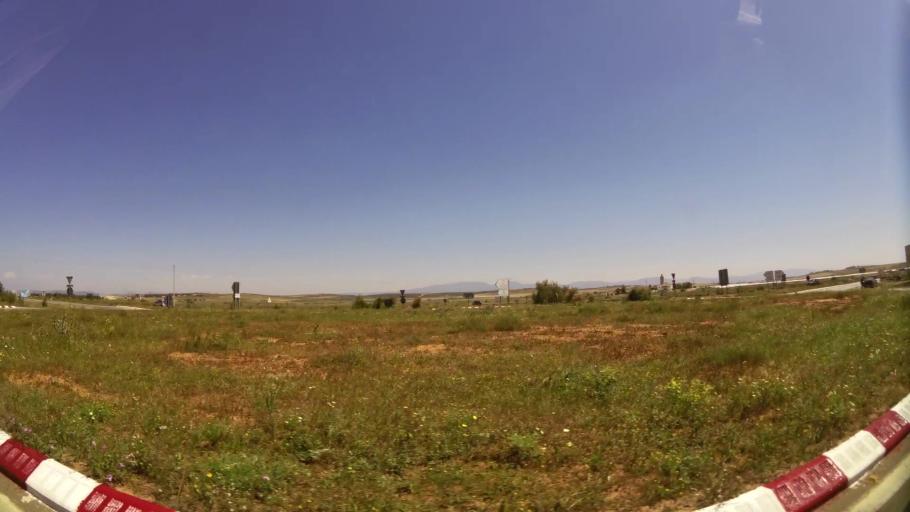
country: MA
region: Oriental
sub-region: Berkane-Taourirt
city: Madagh
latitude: 35.1054
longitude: -2.3512
